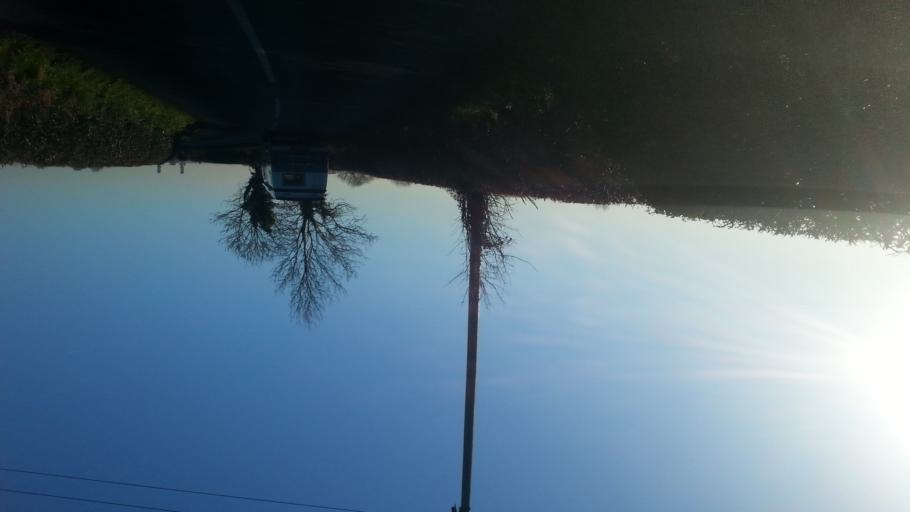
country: GB
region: England
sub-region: Nottinghamshire
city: Newark on Trent
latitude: 53.1031
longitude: -0.8269
